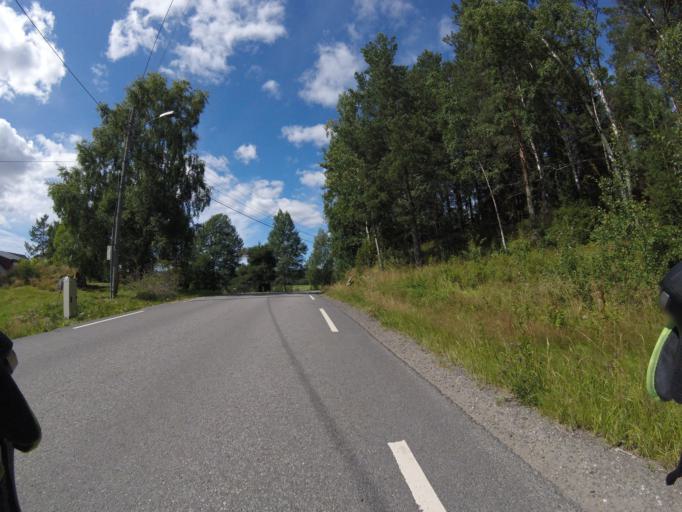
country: NO
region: Akershus
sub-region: Lorenskog
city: Kjenn
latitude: 59.9067
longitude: 10.9609
